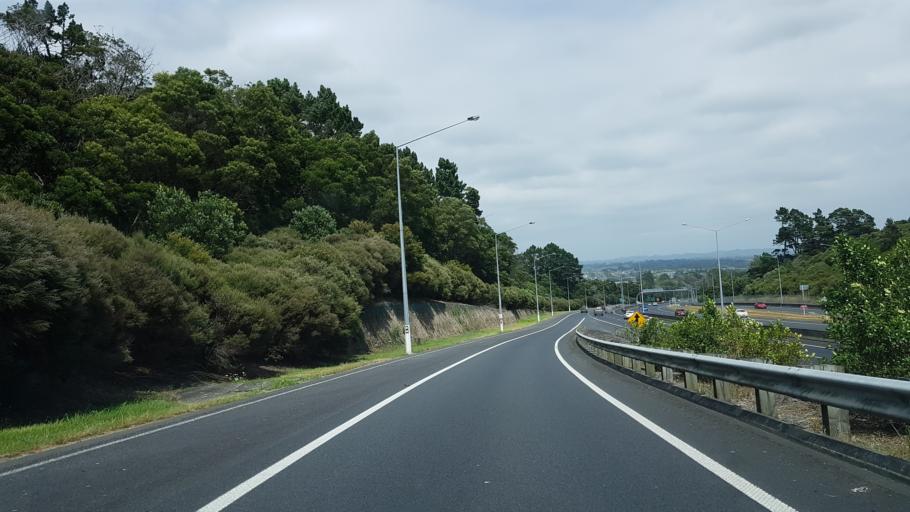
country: NZ
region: Auckland
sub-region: Auckland
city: North Shore
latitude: -36.7819
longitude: 174.6771
